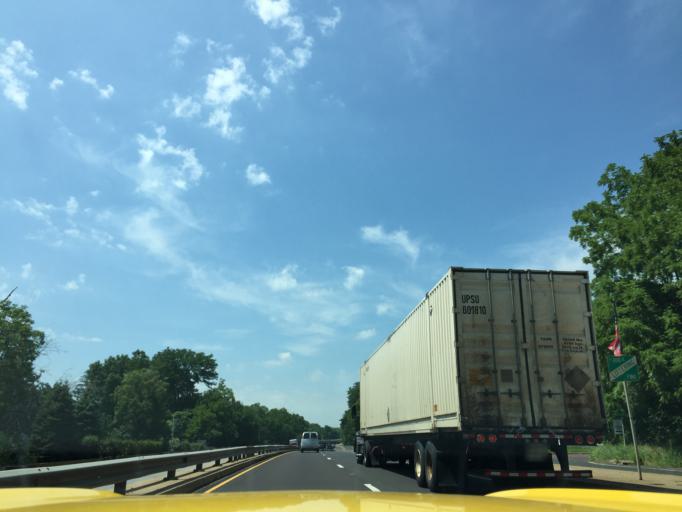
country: US
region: Pennsylvania
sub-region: Bucks County
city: Langhorne Manor
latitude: 40.1703
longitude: -74.9165
